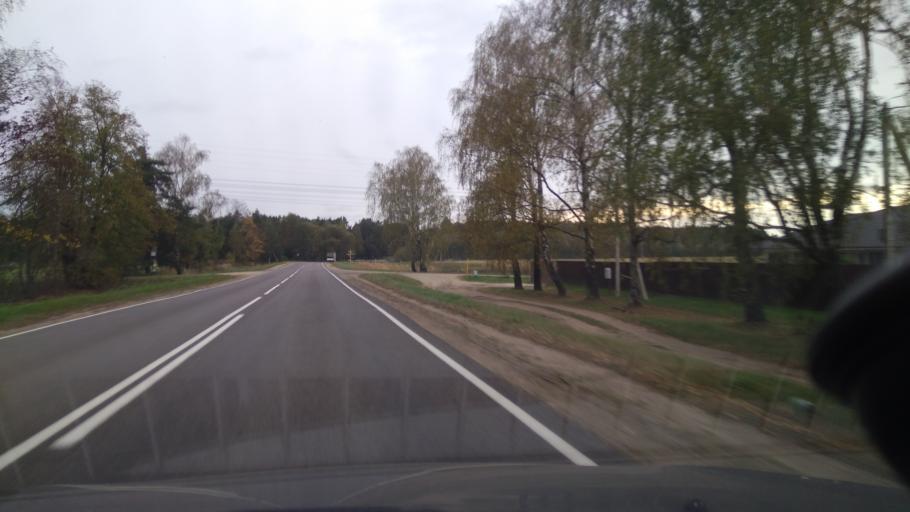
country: BY
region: Minsk
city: Svislach
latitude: 53.6519
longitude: 27.9302
